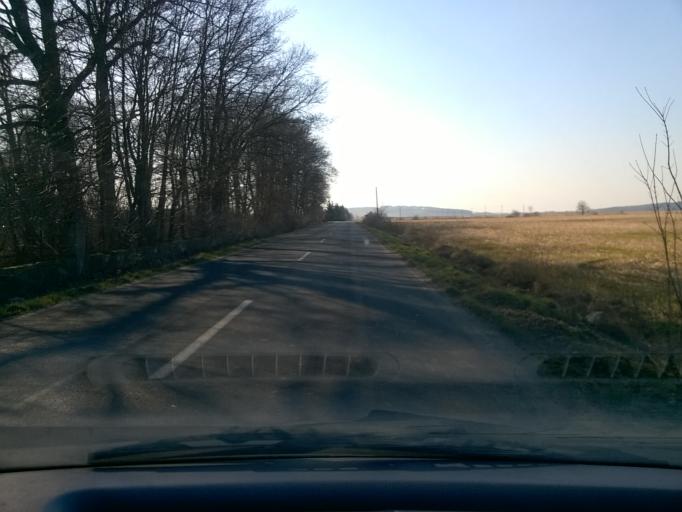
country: PL
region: Kujawsko-Pomorskie
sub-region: Powiat nakielski
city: Kcynia
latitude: 53.0083
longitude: 17.4184
